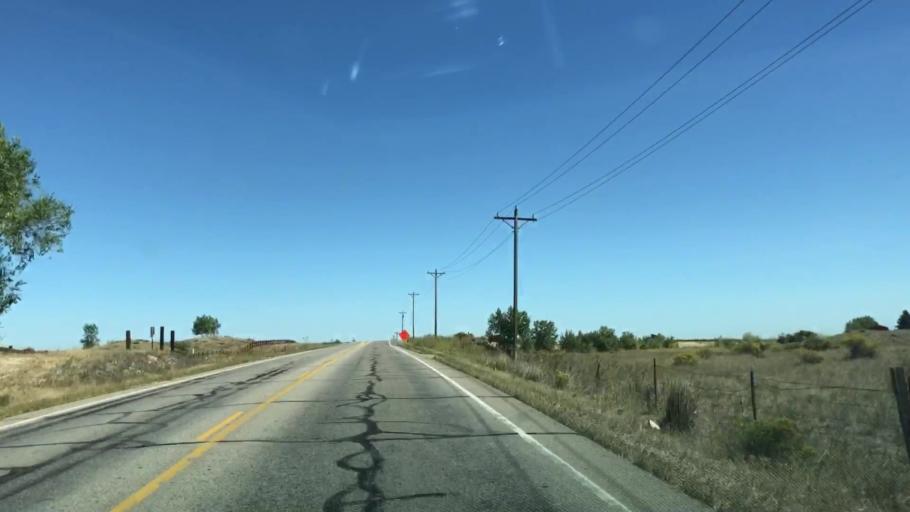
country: US
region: Colorado
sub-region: Weld County
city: Windsor
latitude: 40.5228
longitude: -104.9496
